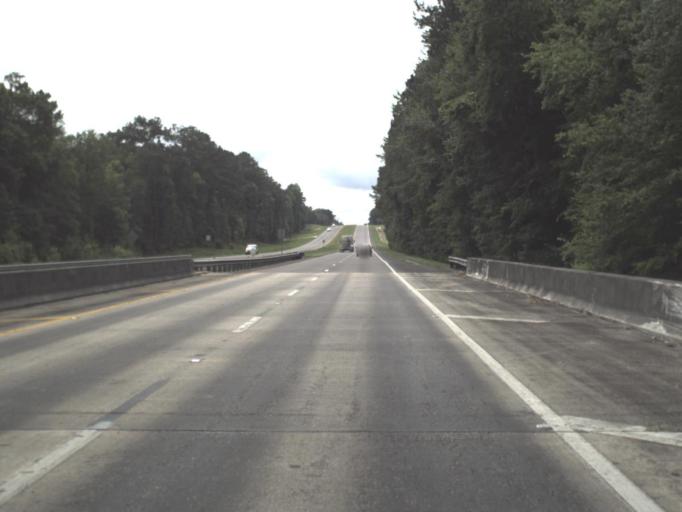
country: US
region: Georgia
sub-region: Charlton County
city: Folkston
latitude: 30.7619
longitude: -81.9673
